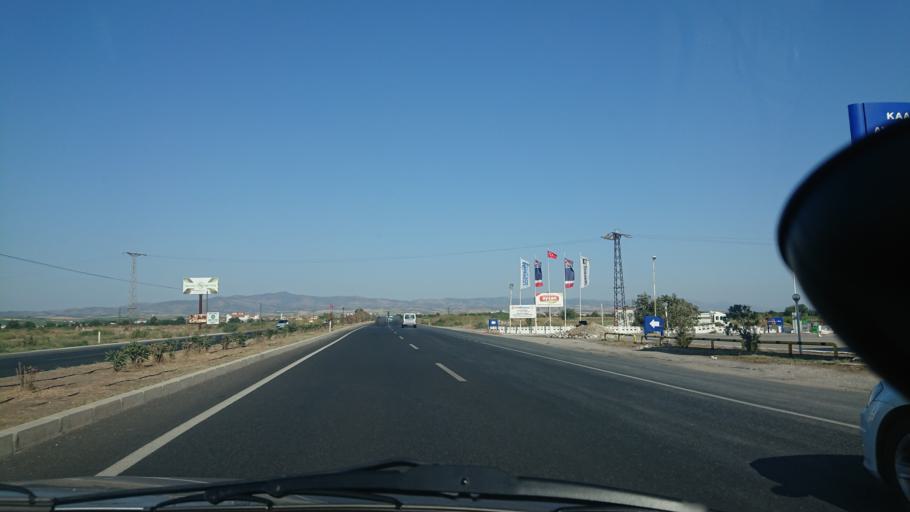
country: TR
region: Manisa
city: Salihli
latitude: 38.5052
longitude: 28.2268
